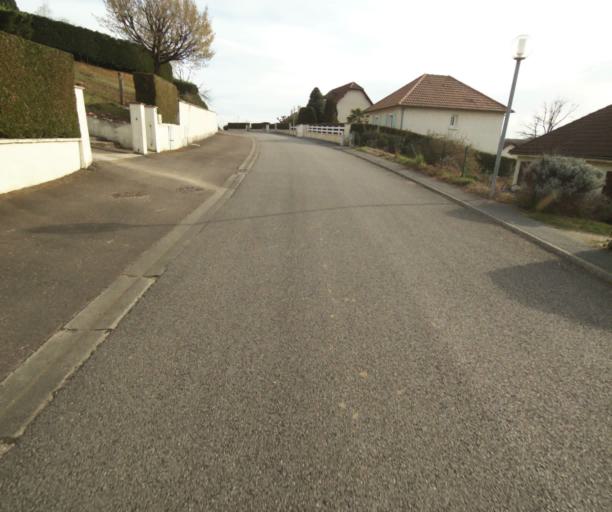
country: FR
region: Limousin
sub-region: Departement de la Correze
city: Naves
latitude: 45.3182
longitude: 1.7591
